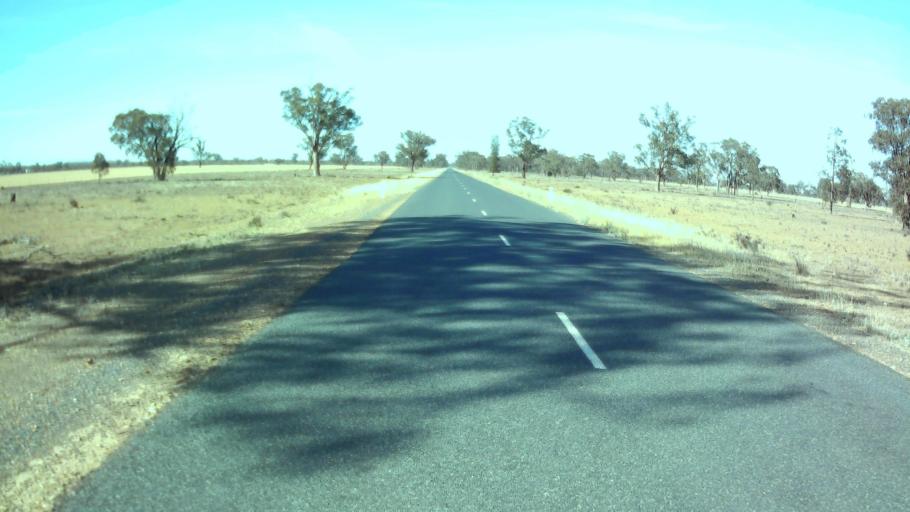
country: AU
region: New South Wales
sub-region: Weddin
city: Grenfell
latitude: -34.0820
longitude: 147.8952
